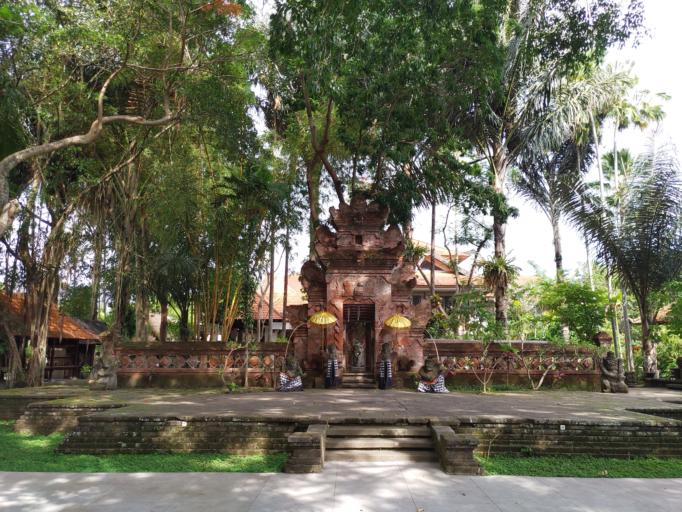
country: ID
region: Bali
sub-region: Kabupaten Gianyar
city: Ubud
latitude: -8.5228
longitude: 115.2641
